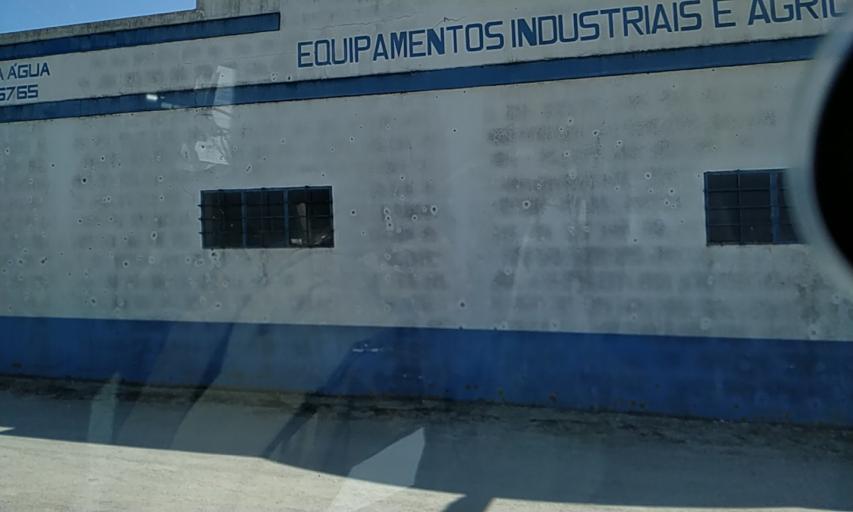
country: PT
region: Setubal
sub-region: Palmela
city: Palmela
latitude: 38.6016
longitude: -8.8031
